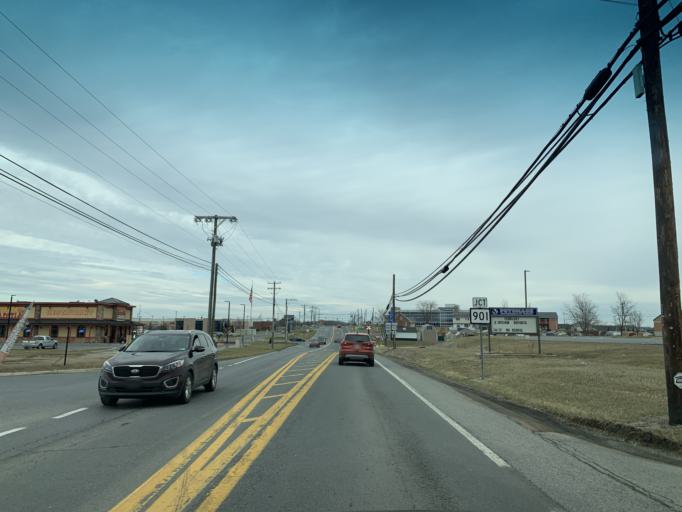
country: US
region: West Virginia
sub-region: Berkeley County
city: Martinsburg
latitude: 39.5410
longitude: -77.9079
